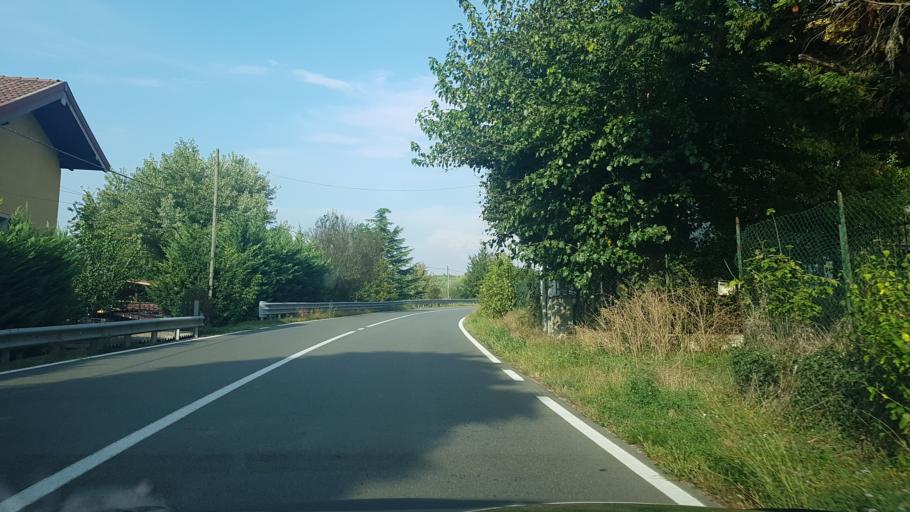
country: IT
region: Piedmont
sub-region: Provincia di Alessandria
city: Bergamasco
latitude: 44.8170
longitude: 8.4587
